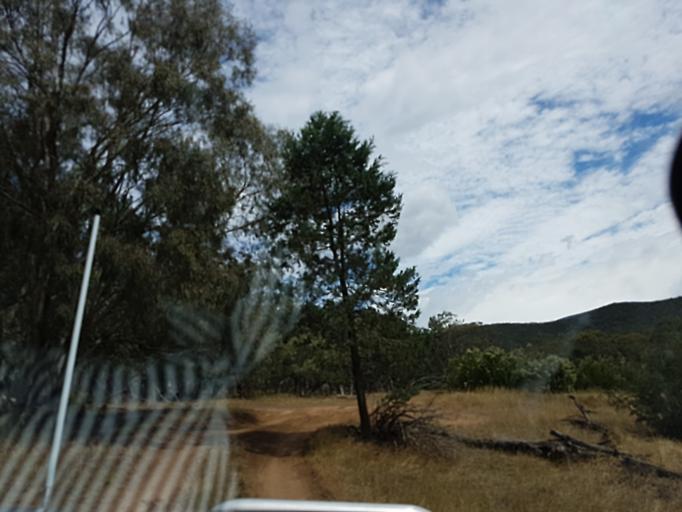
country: AU
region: New South Wales
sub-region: Snowy River
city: Jindabyne
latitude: -36.9469
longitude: 148.3969
